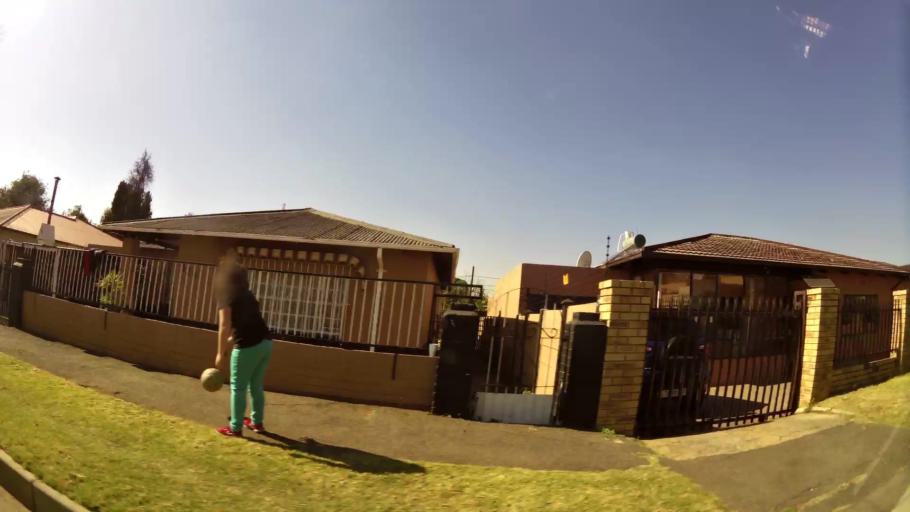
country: ZA
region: Gauteng
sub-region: City of Johannesburg Metropolitan Municipality
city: Johannesburg
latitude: -26.1777
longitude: 27.9644
